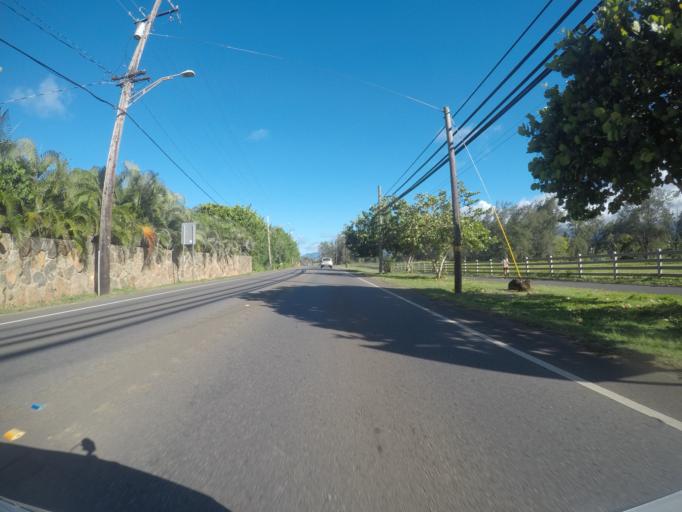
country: US
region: Hawaii
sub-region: Honolulu County
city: Kahuku
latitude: 21.6649
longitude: -157.9367
